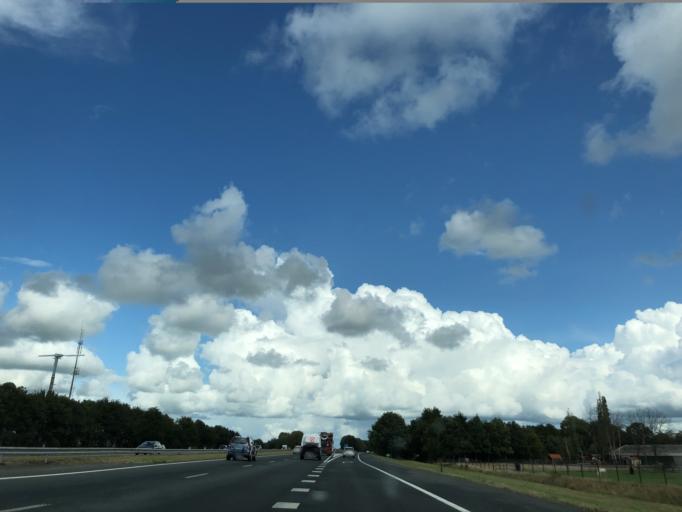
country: NL
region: Groningen
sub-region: Gemeente Grootegast
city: Grootegast
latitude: 53.1506
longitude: 6.2601
